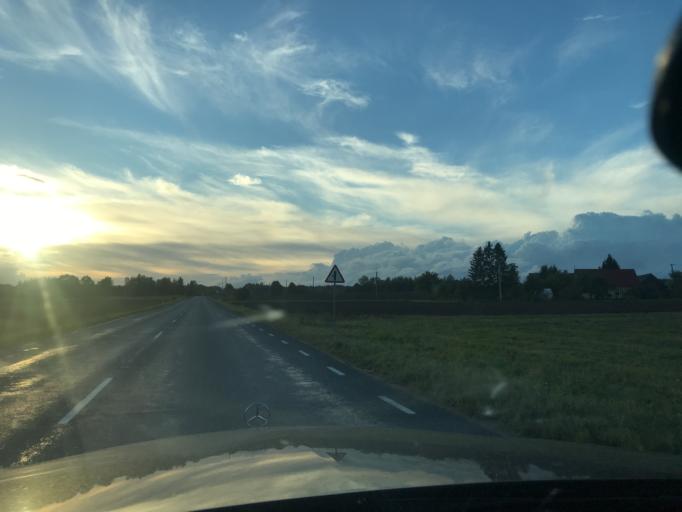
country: EE
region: Vorumaa
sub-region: Antsla vald
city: Vana-Antsla
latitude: 57.8798
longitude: 26.7141
